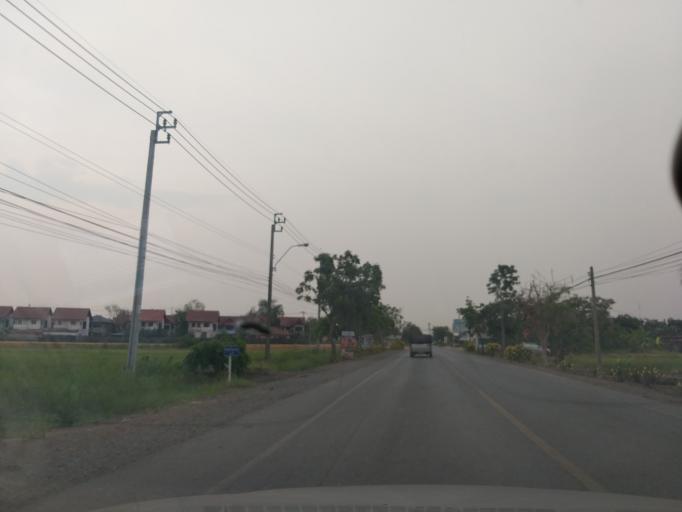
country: TH
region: Bangkok
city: Nong Chok
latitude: 13.8271
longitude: 100.9158
